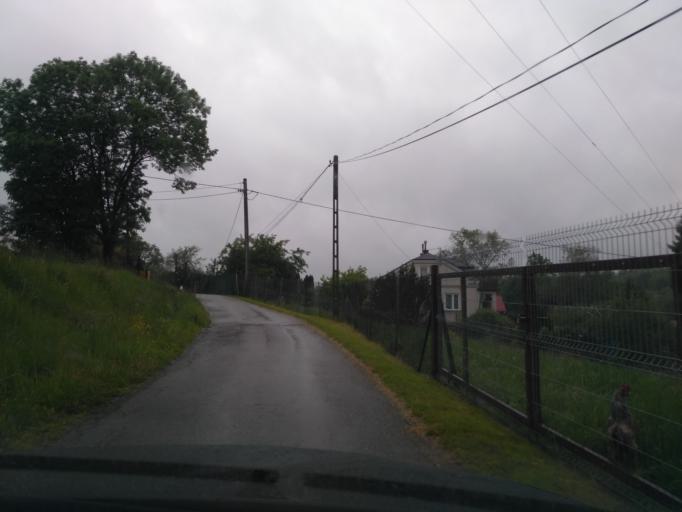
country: PL
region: Lesser Poland Voivodeship
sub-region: Powiat gorlicki
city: Gorlice
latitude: 49.6682
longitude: 21.1379
